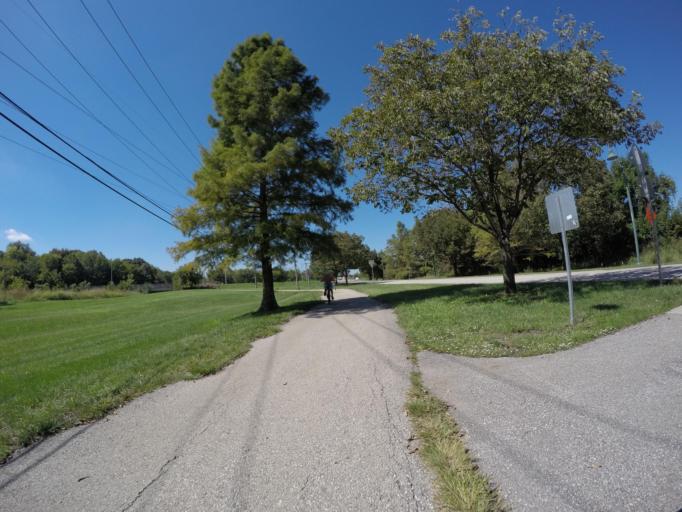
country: US
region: Kansas
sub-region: Johnson County
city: Leawood
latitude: 38.9318
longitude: -94.6284
